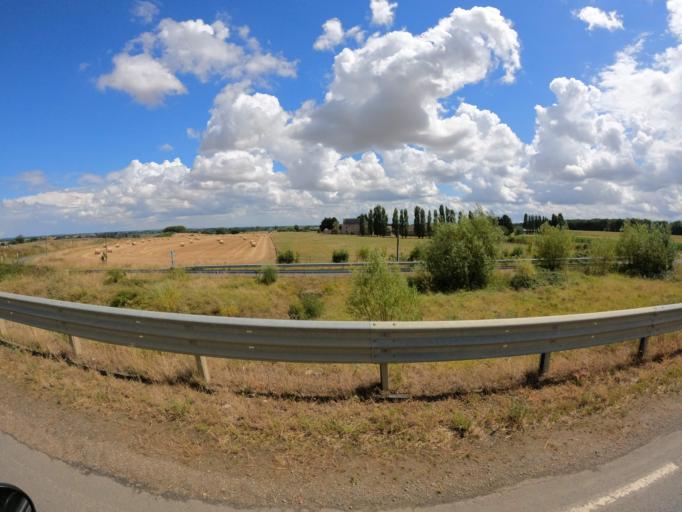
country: FR
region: Pays de la Loire
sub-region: Departement de la Sarthe
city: Juigne-sur-Sarthe
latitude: 47.9093
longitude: -0.2744
